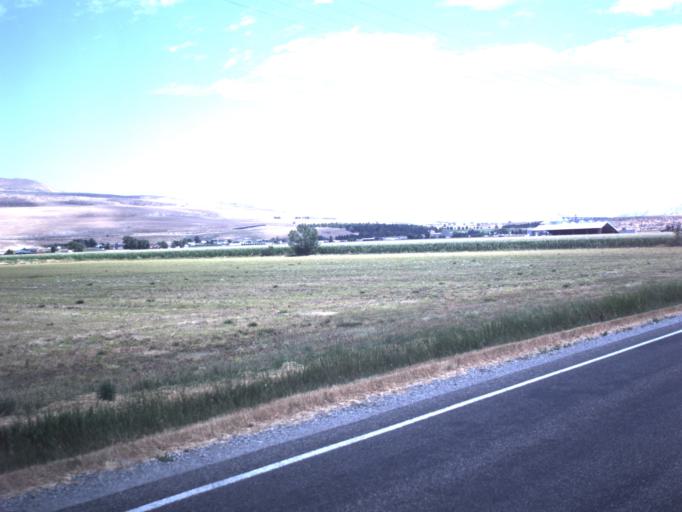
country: US
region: Utah
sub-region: Box Elder County
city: Tremonton
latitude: 41.7097
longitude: -112.2556
